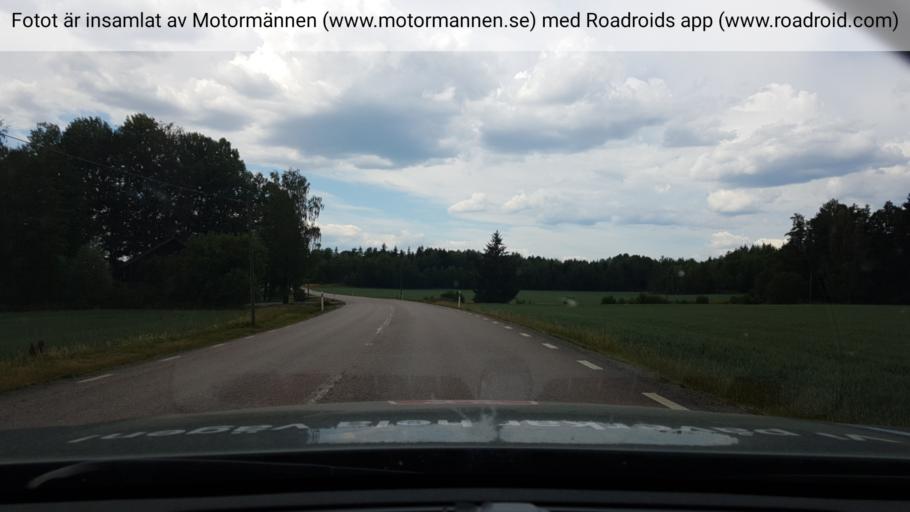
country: SE
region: Uppsala
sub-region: Heby Kommun
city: Heby
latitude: 59.8185
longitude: 16.7762
